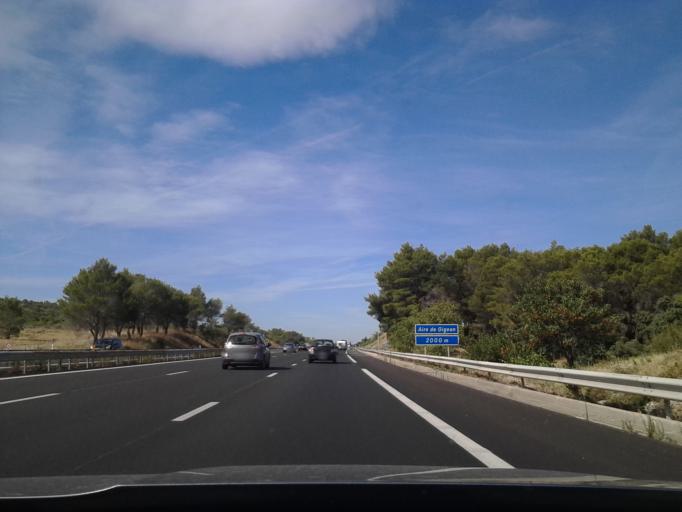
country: FR
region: Languedoc-Roussillon
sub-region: Departement de l'Herault
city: Gigean
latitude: 43.5085
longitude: 3.7402
